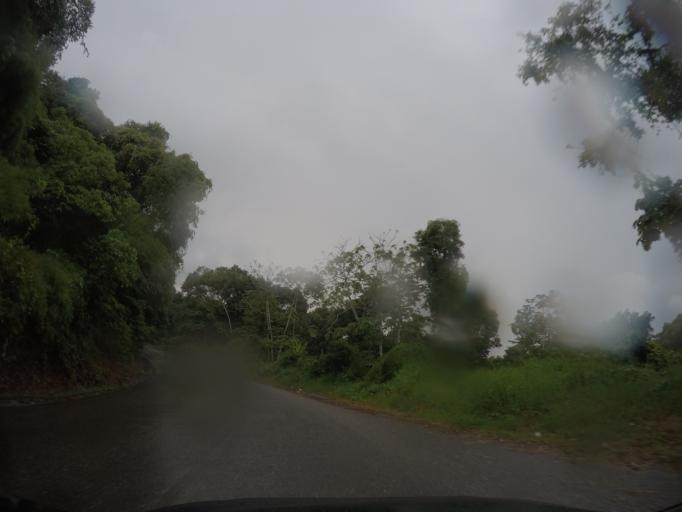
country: MX
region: Oaxaca
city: San Gabriel Mixtepec
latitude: 16.0804
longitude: -97.0854
